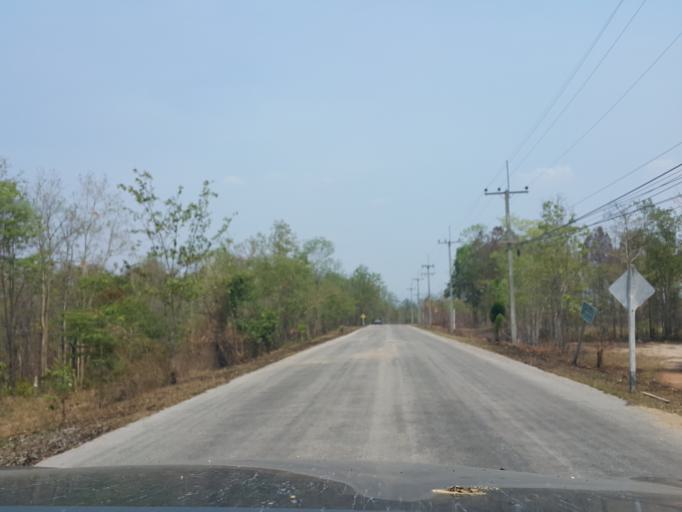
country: TH
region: Lampang
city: Mae Phrik
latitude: 17.5424
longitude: 99.1377
